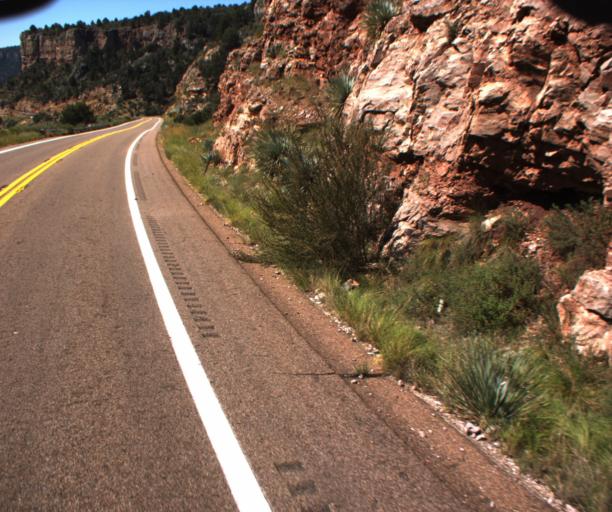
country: US
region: Arizona
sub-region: Navajo County
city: Cibecue
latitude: 33.8201
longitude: -110.4626
